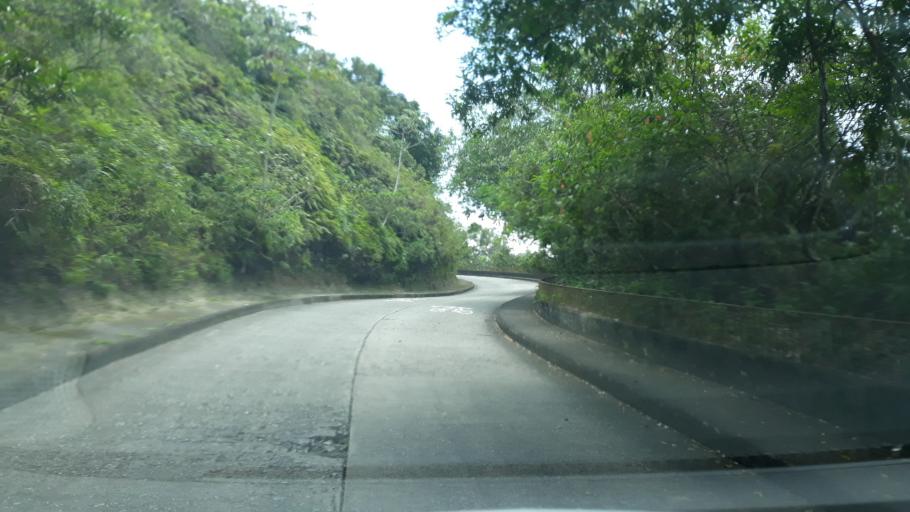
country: BR
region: Rio de Janeiro
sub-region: Rio De Janeiro
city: Rio de Janeiro
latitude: -22.9468
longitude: -43.1979
